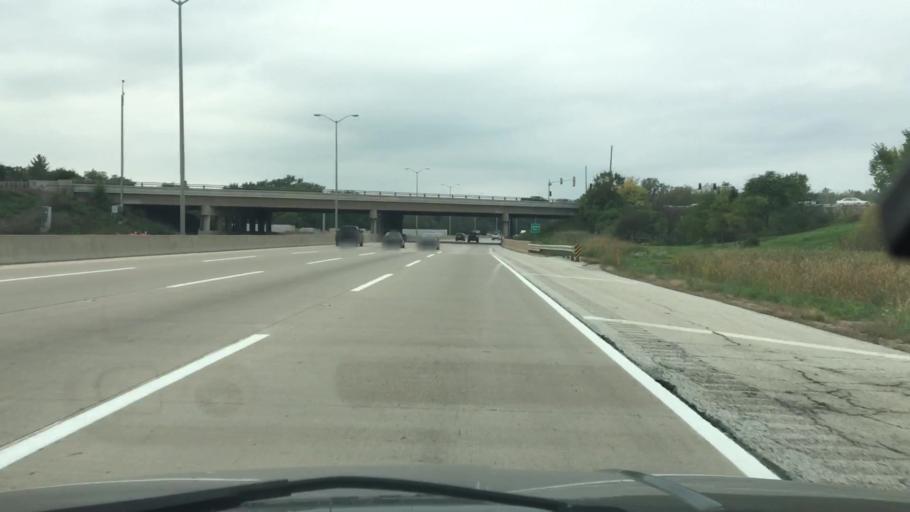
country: US
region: Illinois
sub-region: Cook County
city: Northbrook
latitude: 42.1164
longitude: -87.8764
